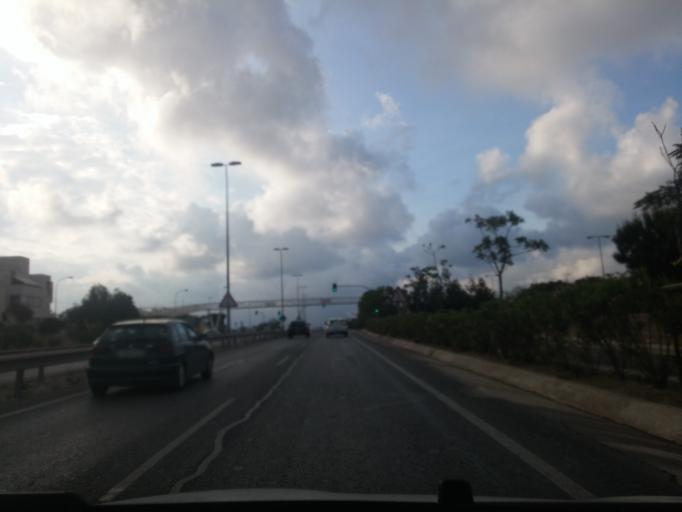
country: ES
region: Valencia
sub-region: Provincia de Alicante
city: Alicante
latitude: 38.3687
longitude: -0.5028
